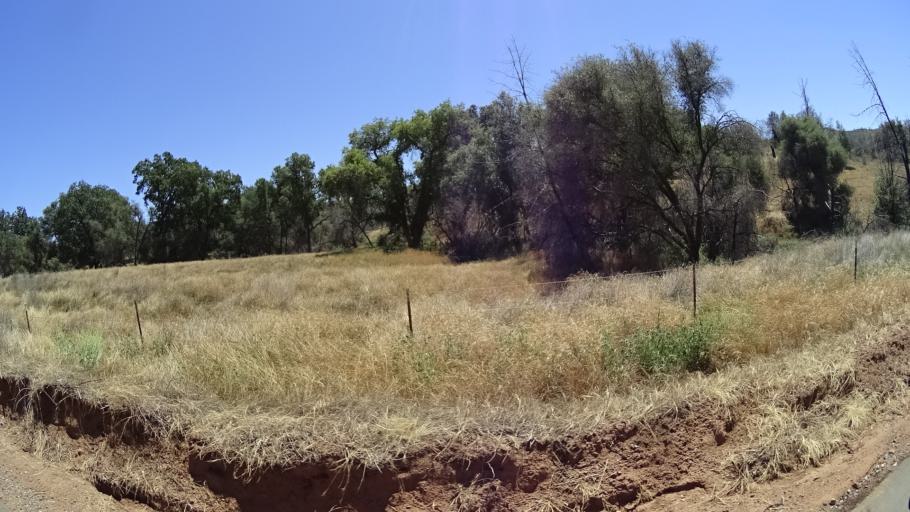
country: US
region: California
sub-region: Calaveras County
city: Mountain Ranch
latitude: 38.2834
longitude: -120.6256
